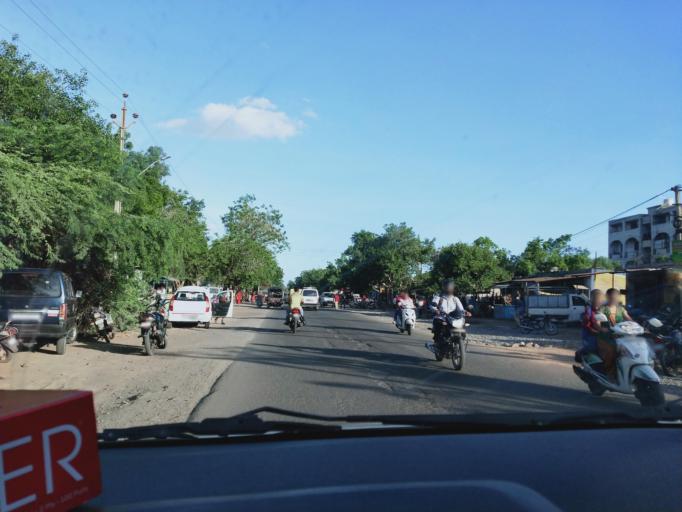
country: IN
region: Gujarat
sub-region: Bhavnagar
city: Bhavnagar
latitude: 21.7419
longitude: 72.1505
